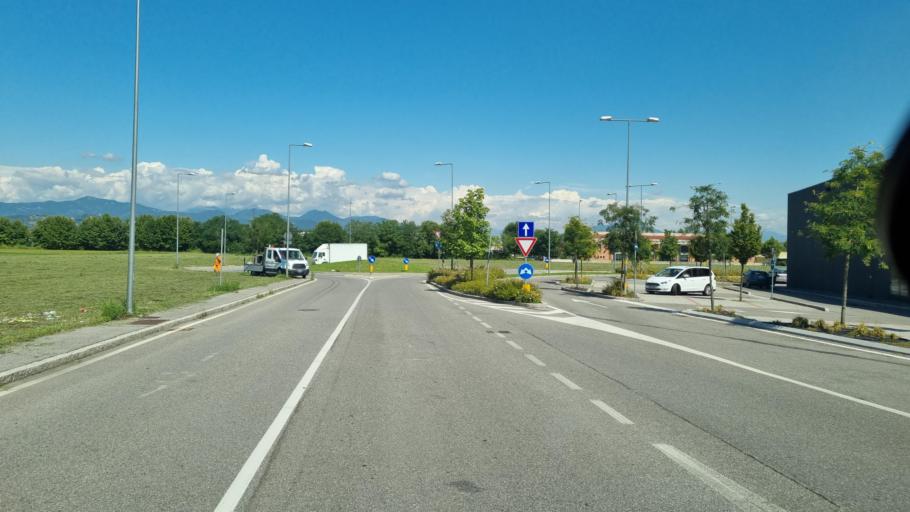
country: IT
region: Lombardy
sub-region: Provincia di Bergamo
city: Lallio
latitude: 45.6545
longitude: 9.6187
